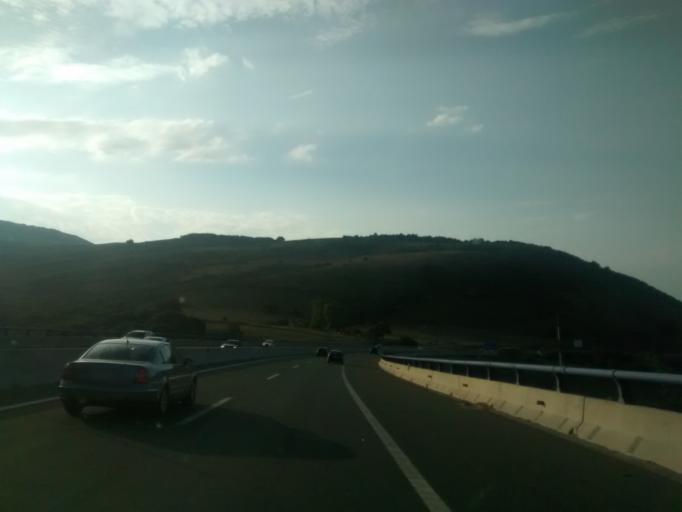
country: ES
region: Cantabria
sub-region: Provincia de Cantabria
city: Santiurde de Reinosa
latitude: 43.0575
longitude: -4.0887
